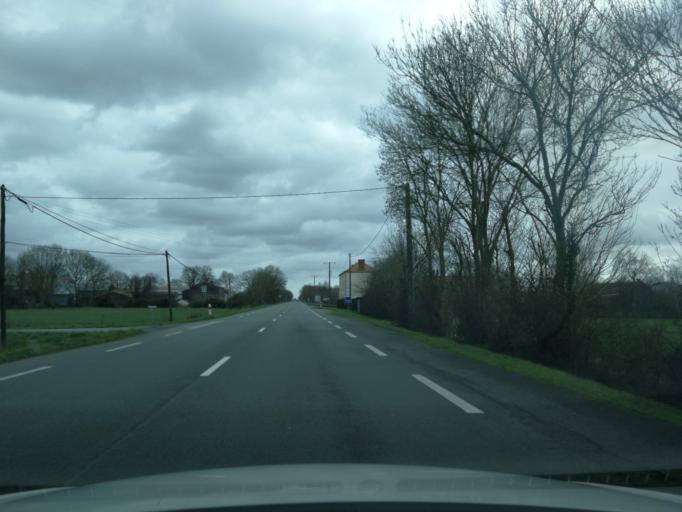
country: FR
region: Pays de la Loire
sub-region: Departement de la Vendee
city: Saint-Georges-de-Montaigu
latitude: 46.9308
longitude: -1.2657
